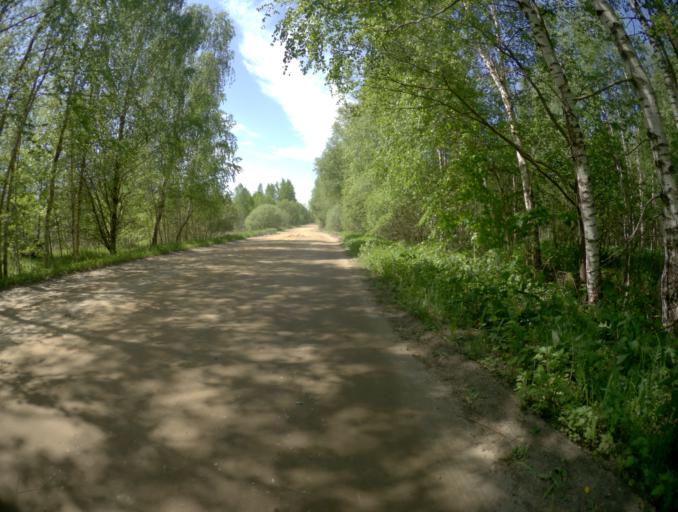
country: RU
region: Vladimir
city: Gusevskiy
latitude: 55.6933
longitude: 40.5460
